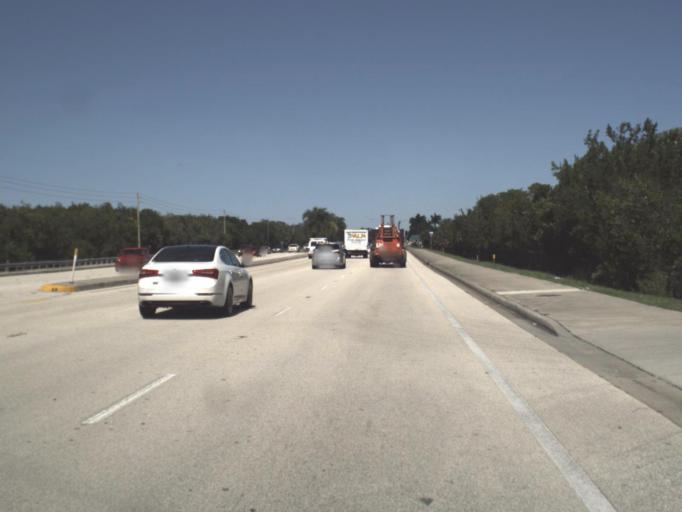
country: US
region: Florida
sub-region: Collier County
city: Naples Park
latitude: 26.2831
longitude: -81.8017
